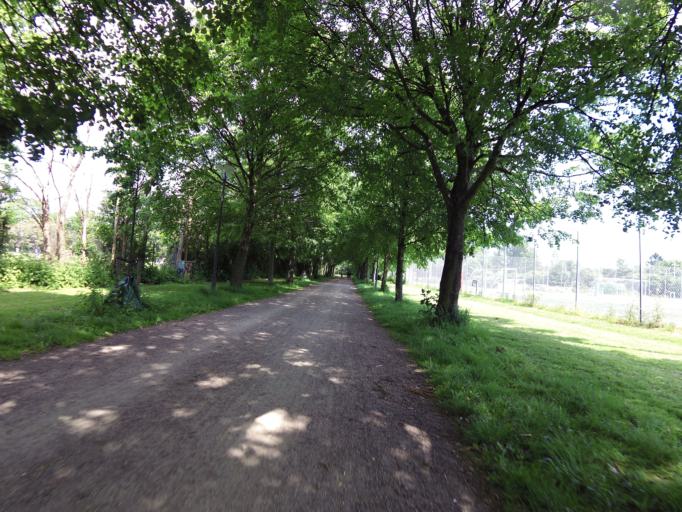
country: DK
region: Capital Region
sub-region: Frederiksberg Kommune
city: Frederiksberg
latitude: 55.7254
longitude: 12.5365
